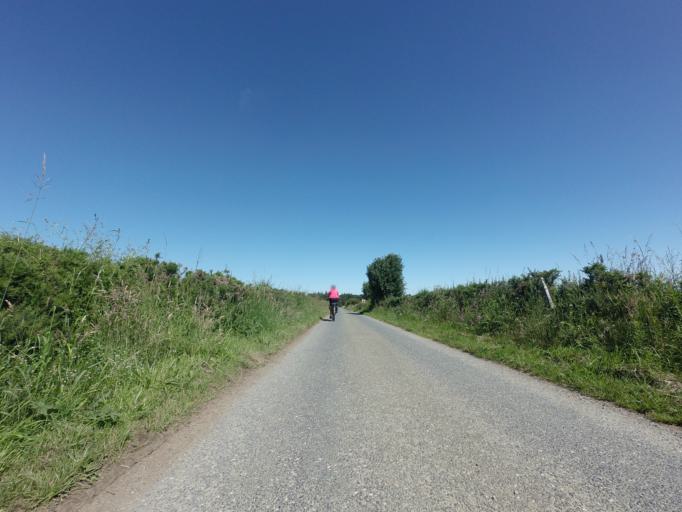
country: GB
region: Scotland
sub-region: Aberdeenshire
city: Macduff
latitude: 57.6288
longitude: -2.4854
